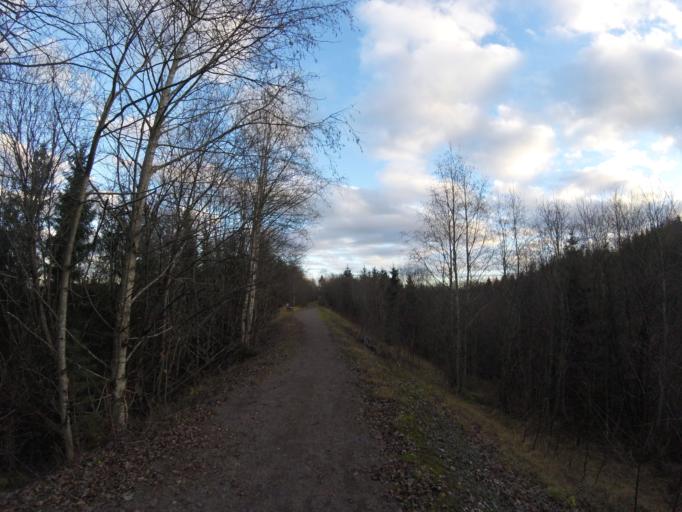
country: NO
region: Akershus
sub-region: Skedsmo
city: Leirsund
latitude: 59.9986
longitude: 11.0669
